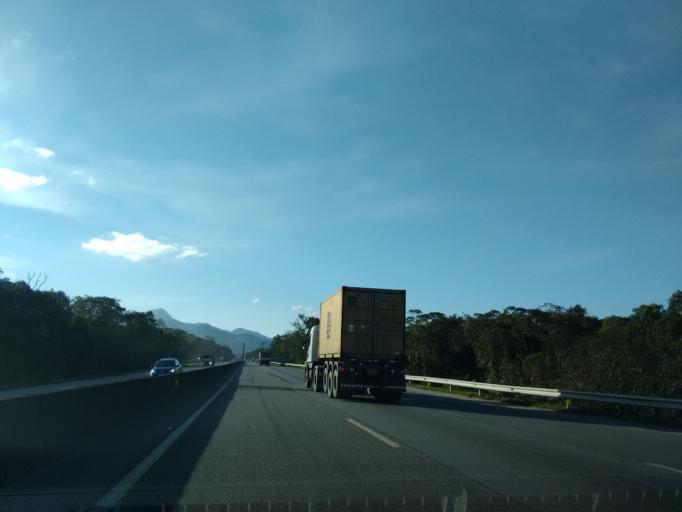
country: BR
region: Santa Catarina
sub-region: Joinville
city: Joinville
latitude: -26.0621
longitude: -48.8600
